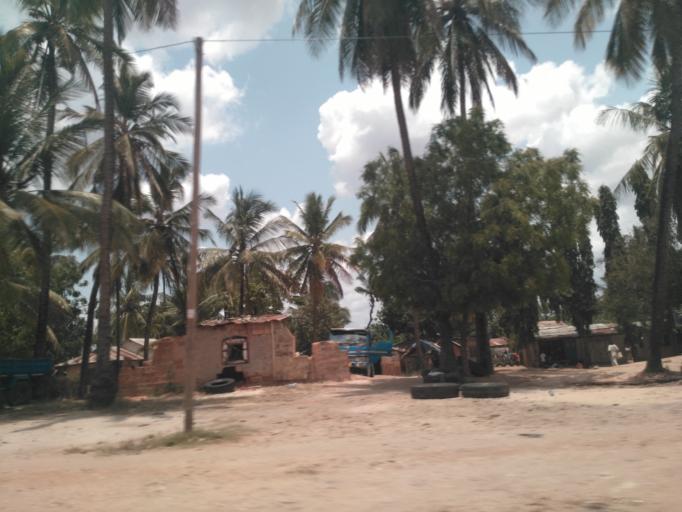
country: TZ
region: Dar es Salaam
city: Dar es Salaam
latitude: -6.8438
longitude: 39.3529
